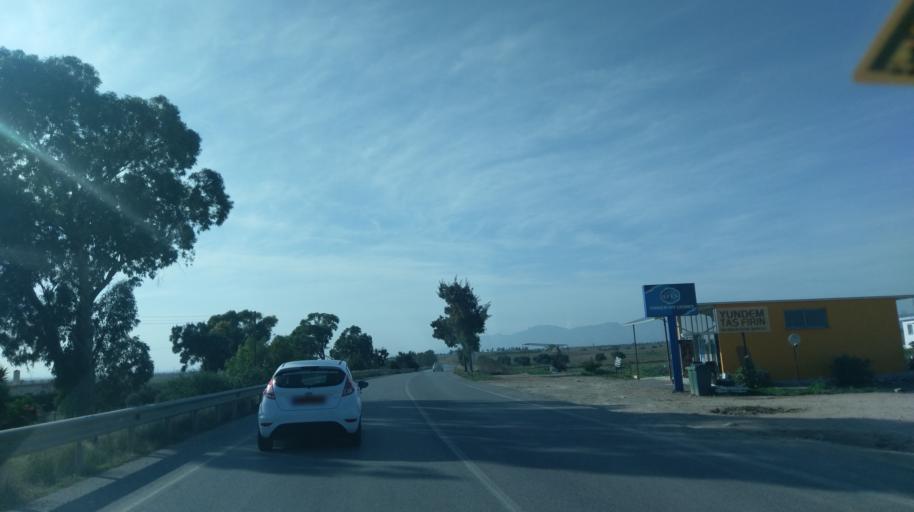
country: CY
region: Ammochostos
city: Lefkonoiko
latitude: 35.2613
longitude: 33.7789
